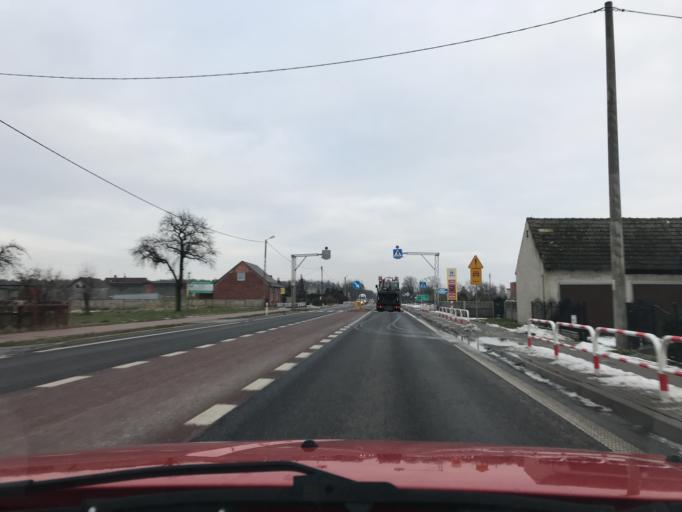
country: PL
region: Greater Poland Voivodeship
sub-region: Powiat pleszewski
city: Goluchow
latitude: 51.8655
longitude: 17.9017
